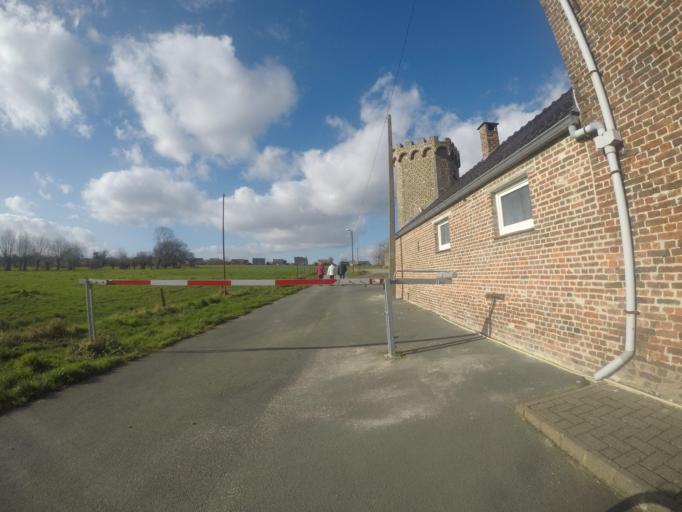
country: BE
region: Wallonia
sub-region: Province du Brabant Wallon
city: Rebecq-Rognon
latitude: 50.6850
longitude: 4.1228
